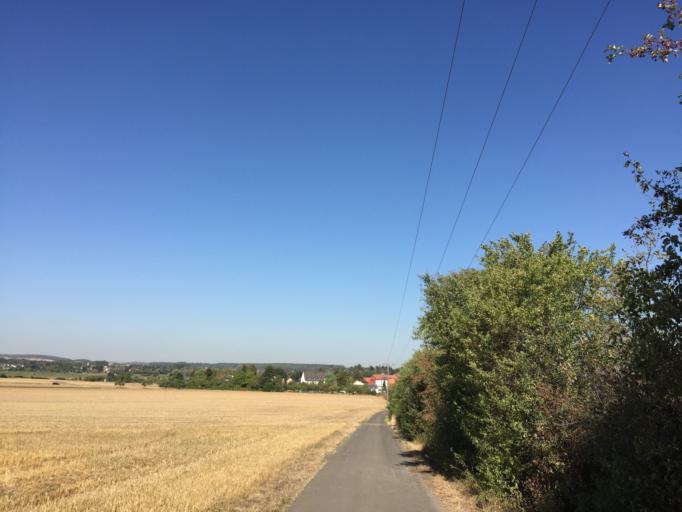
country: DE
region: Hesse
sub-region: Regierungsbezirk Giessen
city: Hungen
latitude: 50.4373
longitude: 8.9277
